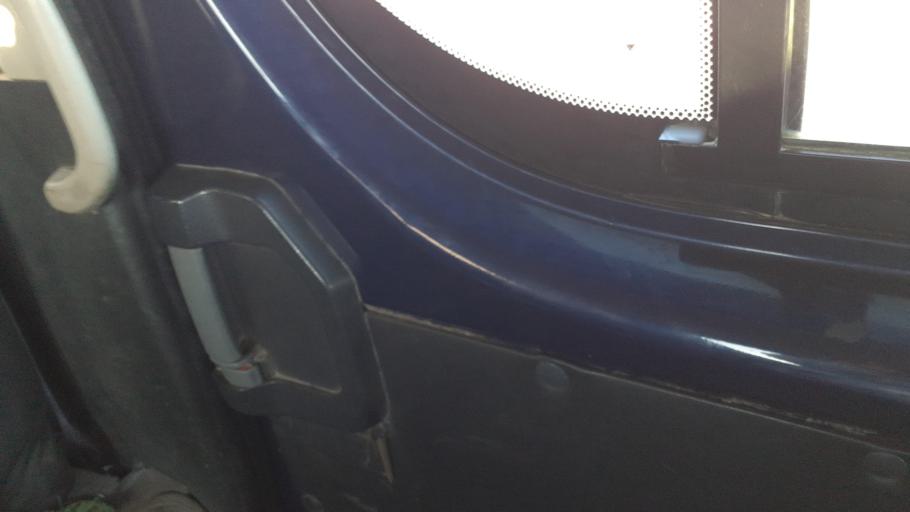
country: BO
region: La Paz
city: Tiahuanaco
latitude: -16.8834
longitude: -68.6817
